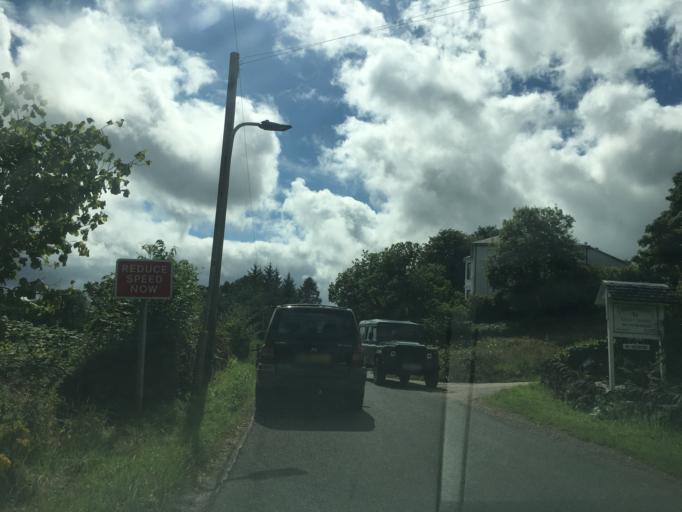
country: GB
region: Scotland
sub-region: Argyll and Bute
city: Port Bannatyne
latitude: 55.9062
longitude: -5.2373
